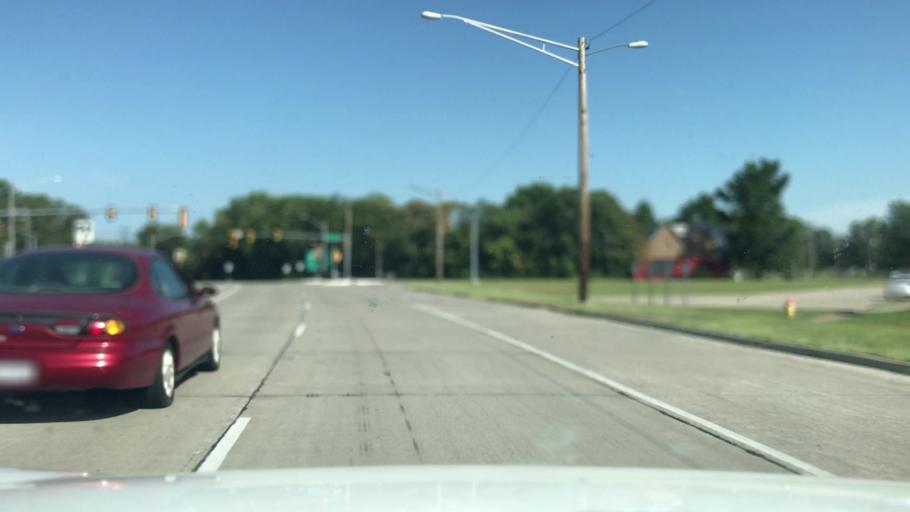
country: US
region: Illinois
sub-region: Madison County
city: Venice
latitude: 38.6703
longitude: -90.1712
